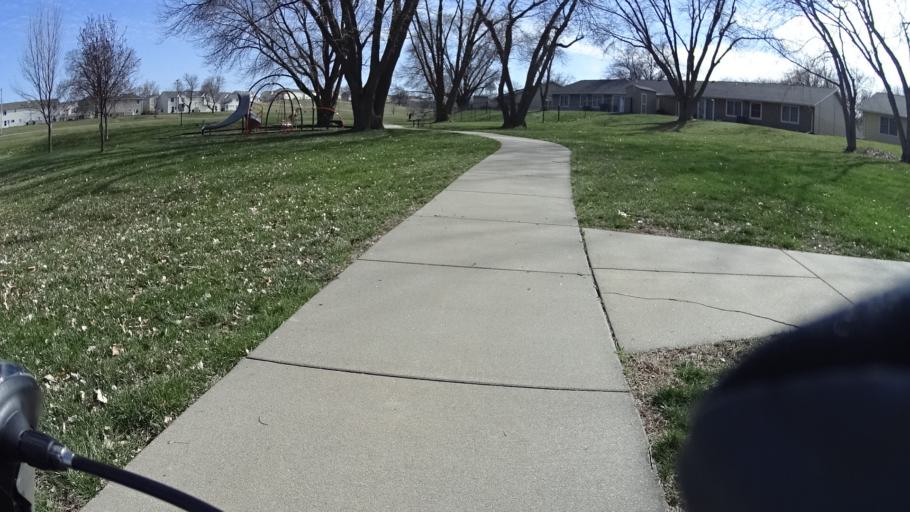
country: US
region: Nebraska
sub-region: Sarpy County
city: Offutt Air Force Base
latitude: 41.1283
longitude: -95.9543
